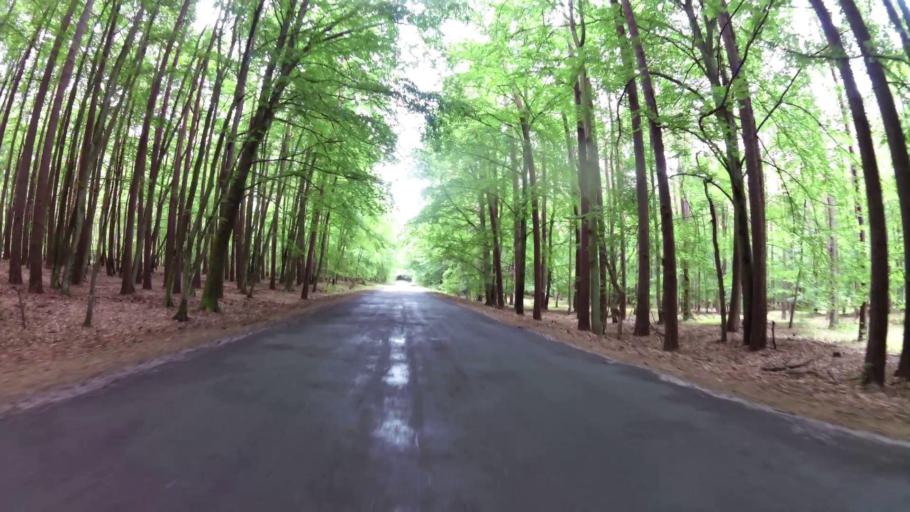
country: PL
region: West Pomeranian Voivodeship
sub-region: Powiat kamienski
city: Miedzyzdroje
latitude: 53.9433
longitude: 14.5509
